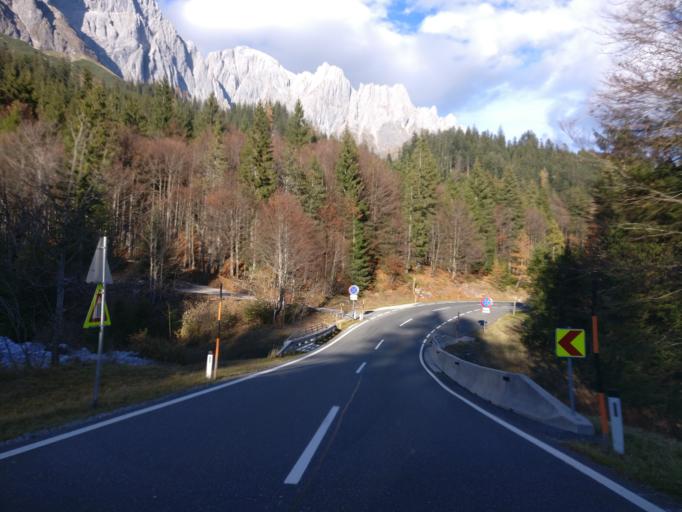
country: AT
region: Salzburg
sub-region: Politischer Bezirk Sankt Johann im Pongau
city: Muhlbach am Hochkonig
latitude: 47.3942
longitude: 13.0806
